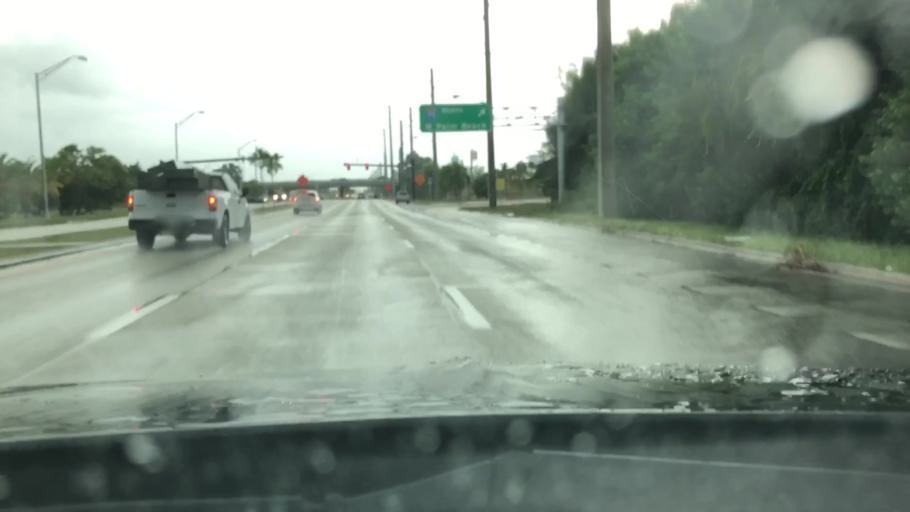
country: US
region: Florida
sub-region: Broward County
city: Kendall Green
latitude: 26.2606
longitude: -80.1295
